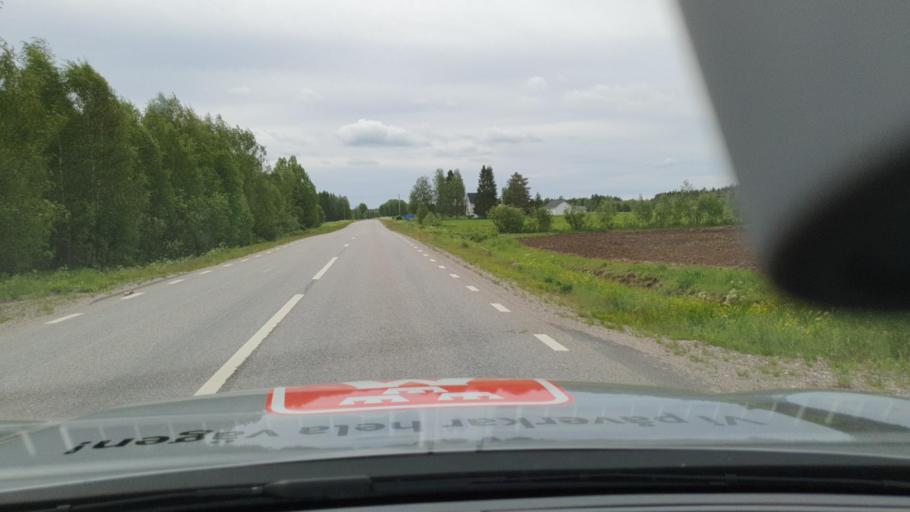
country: SE
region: Norrbotten
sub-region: Kalix Kommun
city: Kalix
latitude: 65.9772
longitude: 23.4604
